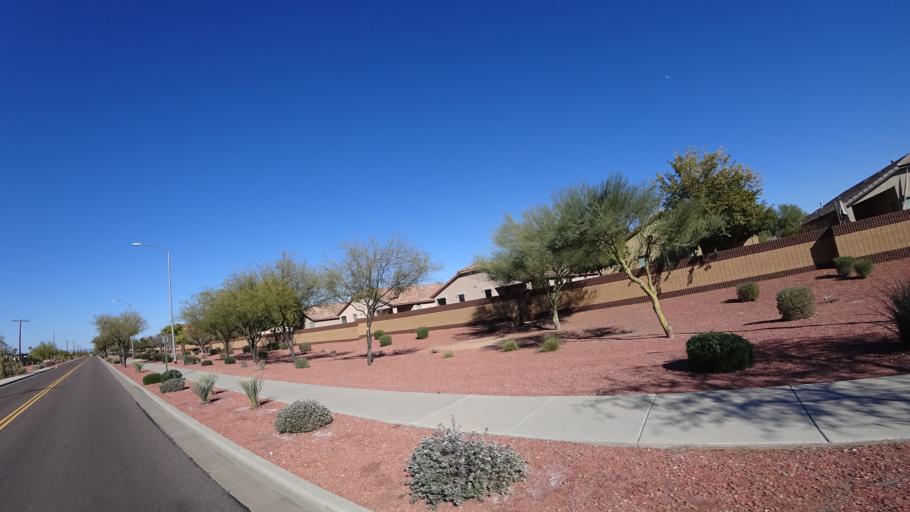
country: US
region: Arizona
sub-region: Maricopa County
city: Sun City West
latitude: 33.6422
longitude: -112.4267
